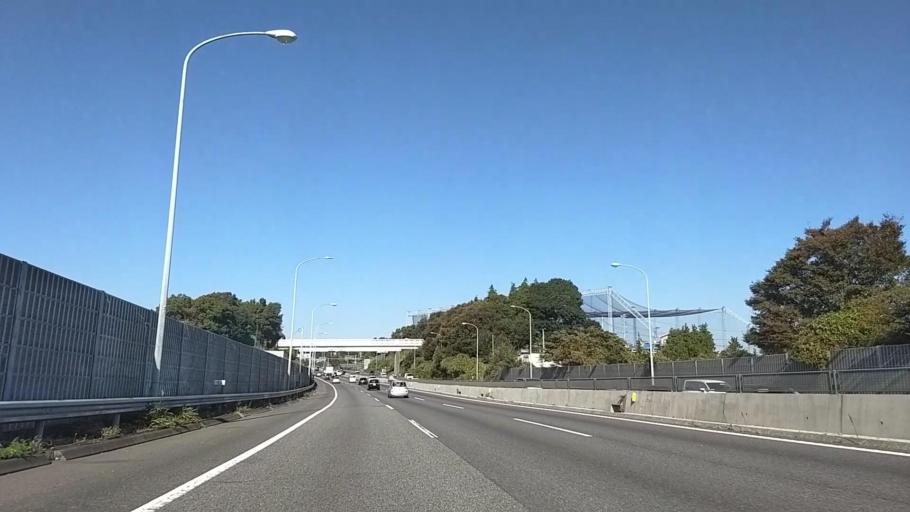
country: JP
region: Kanagawa
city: Minami-rinkan
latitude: 35.4755
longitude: 139.5279
